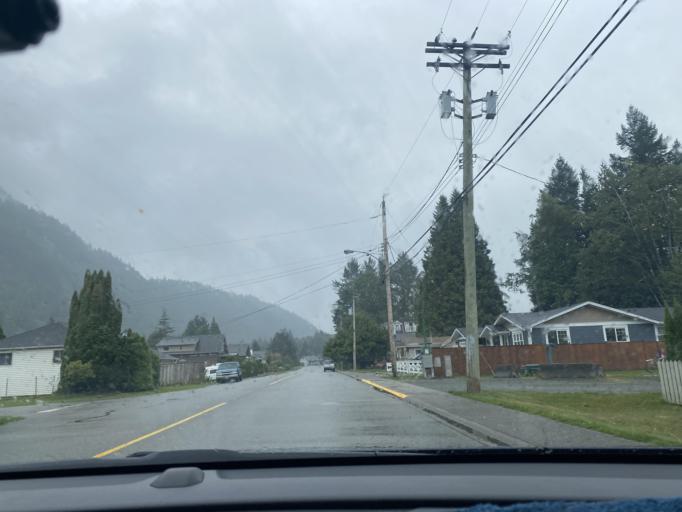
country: CA
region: British Columbia
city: Agassiz
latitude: 49.3020
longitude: -121.7785
